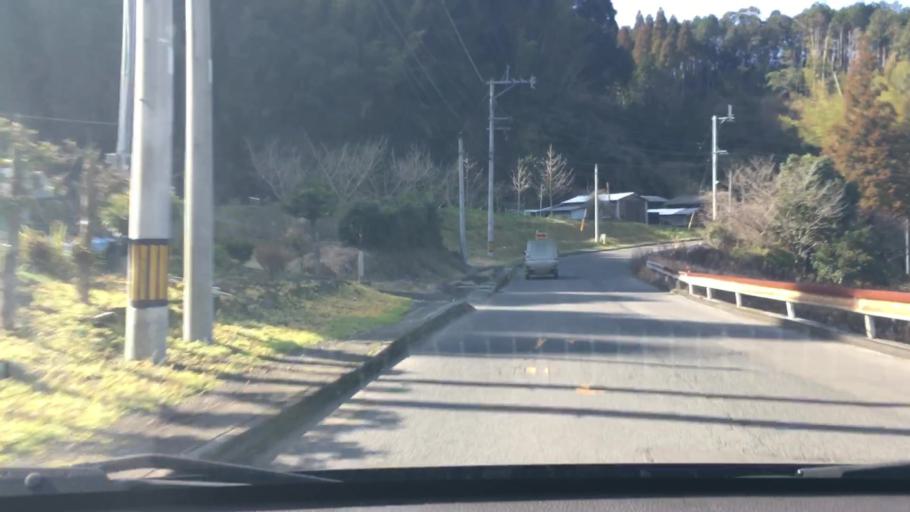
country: JP
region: Kagoshima
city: Ijuin
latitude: 31.7361
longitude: 130.4128
